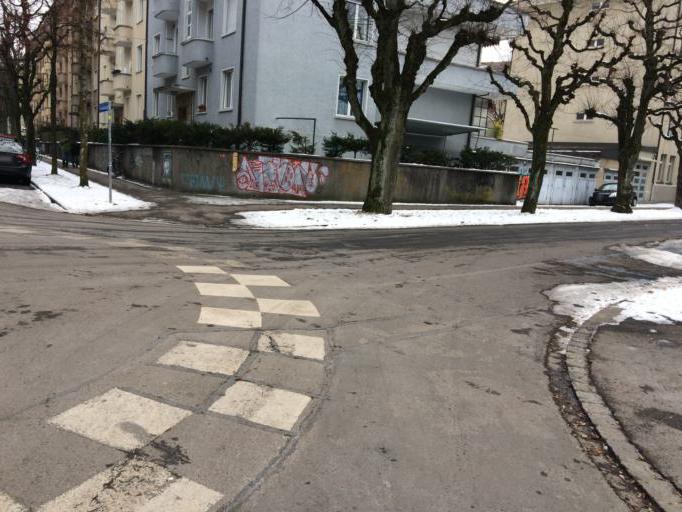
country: CH
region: Bern
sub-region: Bern-Mittelland District
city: Bern
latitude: 46.9549
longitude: 7.4554
